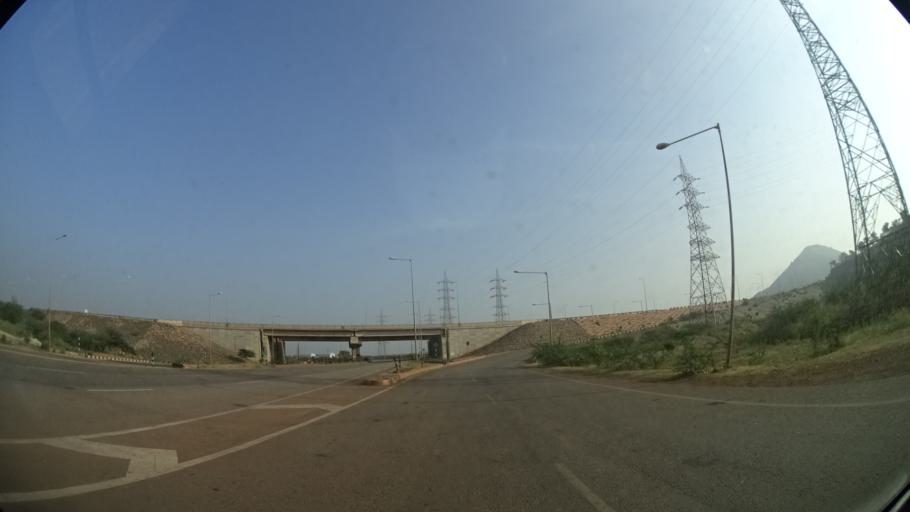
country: IN
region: Karnataka
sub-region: Bellary
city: Hospet
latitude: 15.2483
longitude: 76.3643
